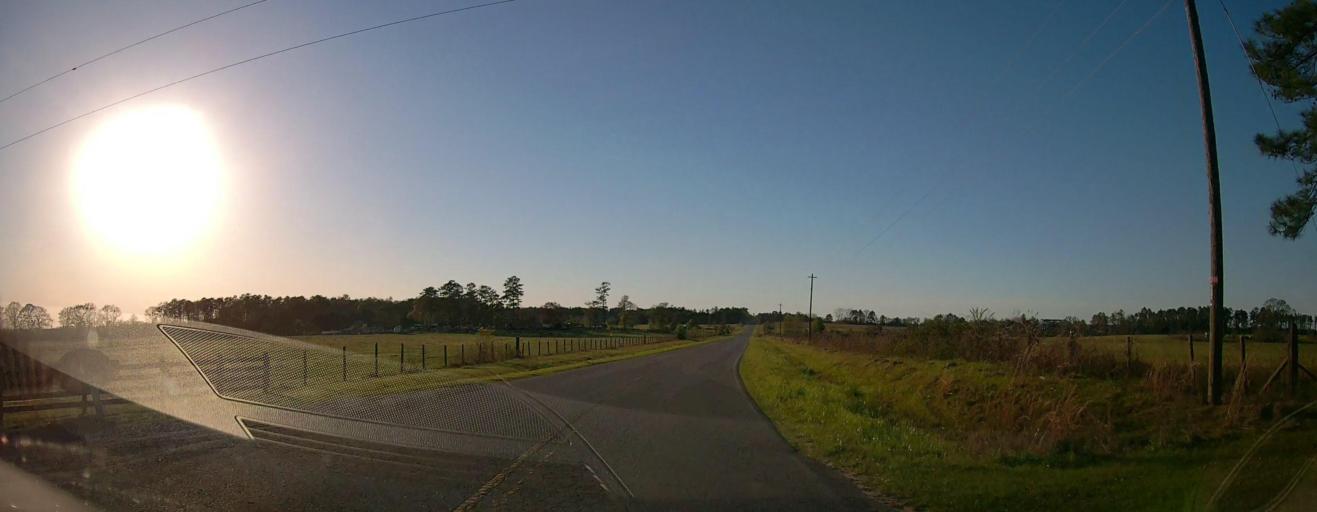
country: US
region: Georgia
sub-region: Wilkinson County
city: Gordon
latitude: 32.8834
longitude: -83.2914
